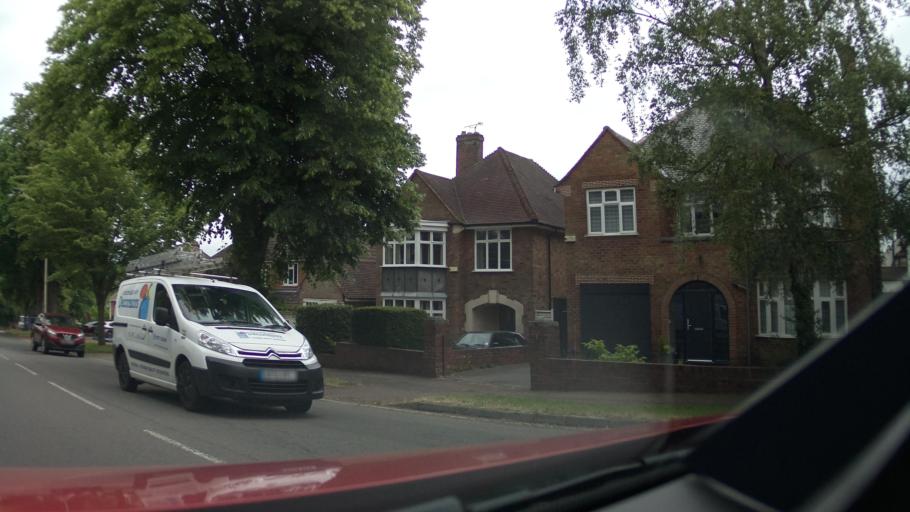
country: GB
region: England
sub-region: Leicestershire
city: Oadby
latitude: 52.6149
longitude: -1.1025
